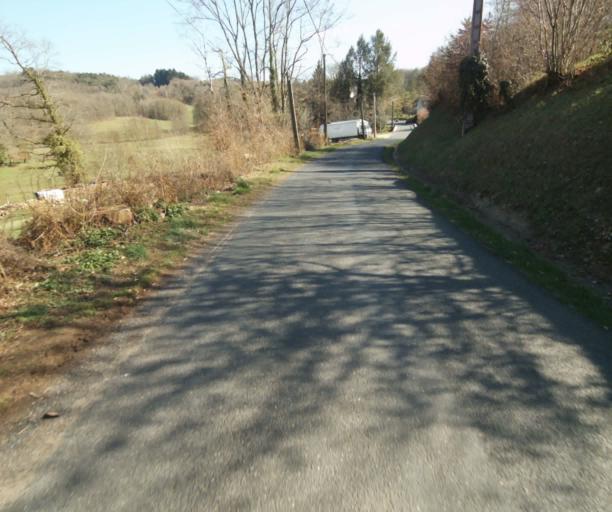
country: FR
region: Limousin
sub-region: Departement de la Correze
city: Saint-Mexant
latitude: 45.2940
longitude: 1.6161
